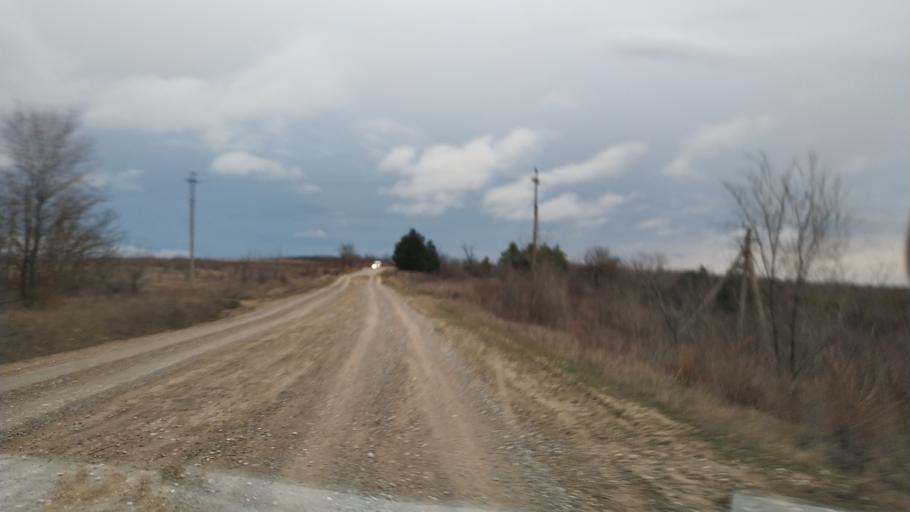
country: MD
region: Causeni
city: Causeni
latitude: 46.6150
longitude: 29.3967
